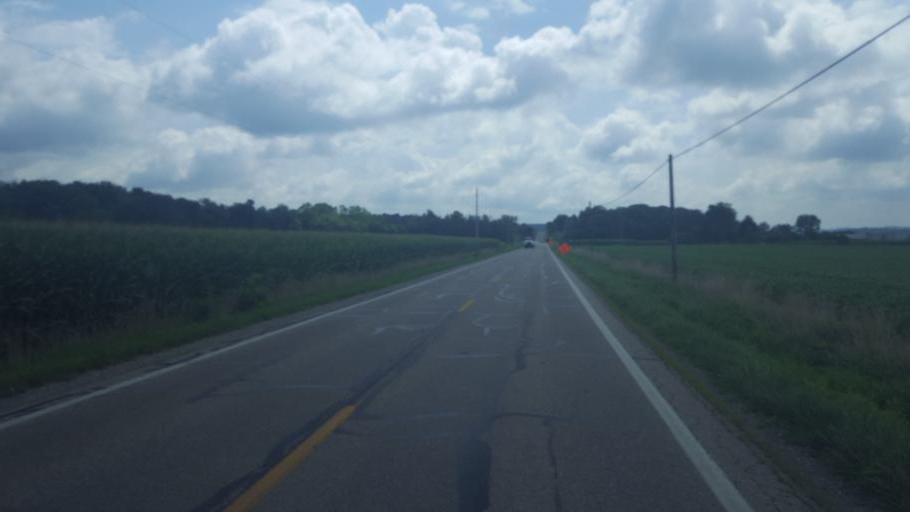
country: US
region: Ohio
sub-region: Ross County
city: Kingston
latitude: 39.4980
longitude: -82.7686
